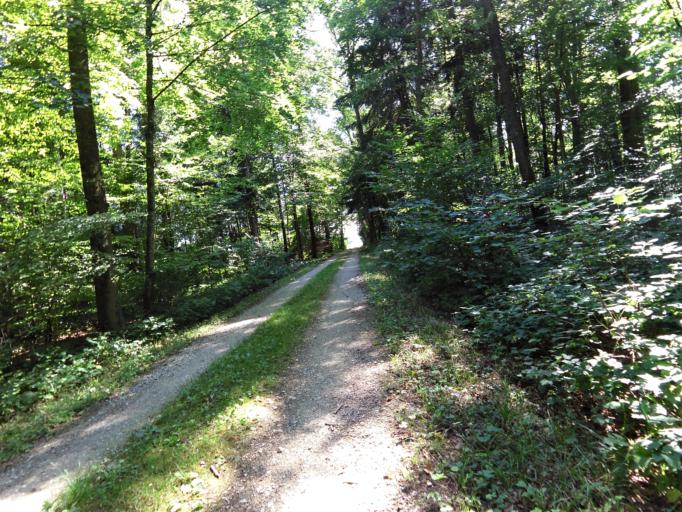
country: CH
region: Thurgau
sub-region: Kreuzlingen District
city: Tagerwilen
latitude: 47.6270
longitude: 9.1323
